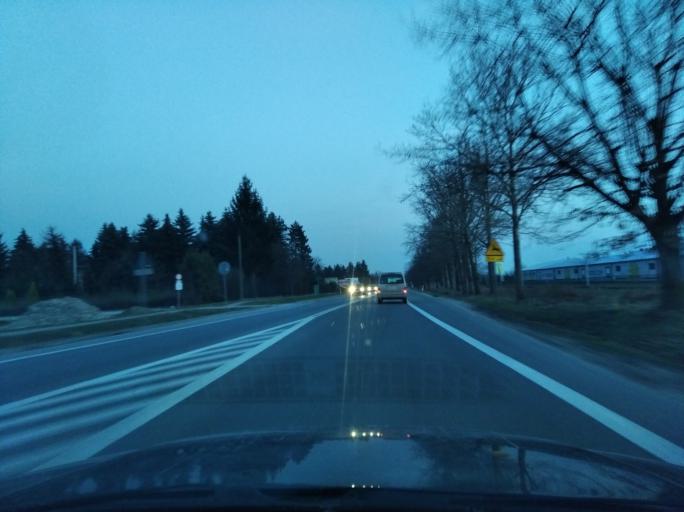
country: PL
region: Subcarpathian Voivodeship
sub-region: Powiat rzeszowski
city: Rudna Mala
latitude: 50.1046
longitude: 21.9766
